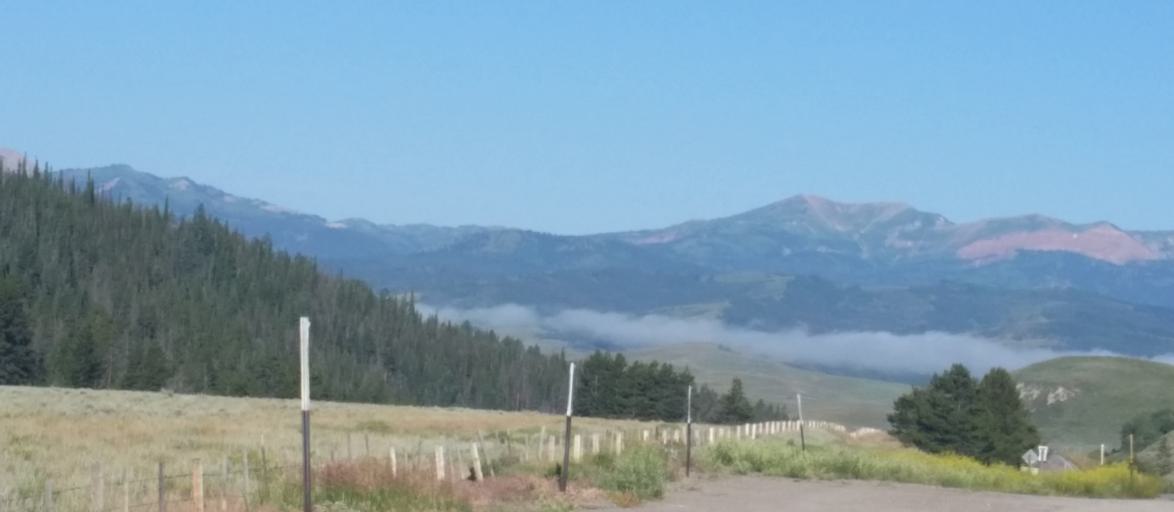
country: US
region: Wyoming
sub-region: Teton County
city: Hoback
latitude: 43.1557
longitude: -110.3025
